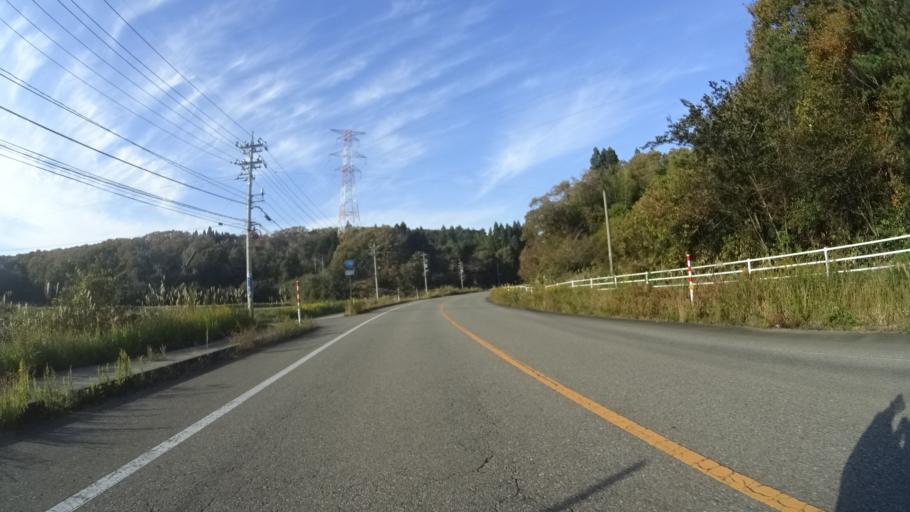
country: JP
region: Ishikawa
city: Hakui
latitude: 37.0470
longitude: 136.7745
